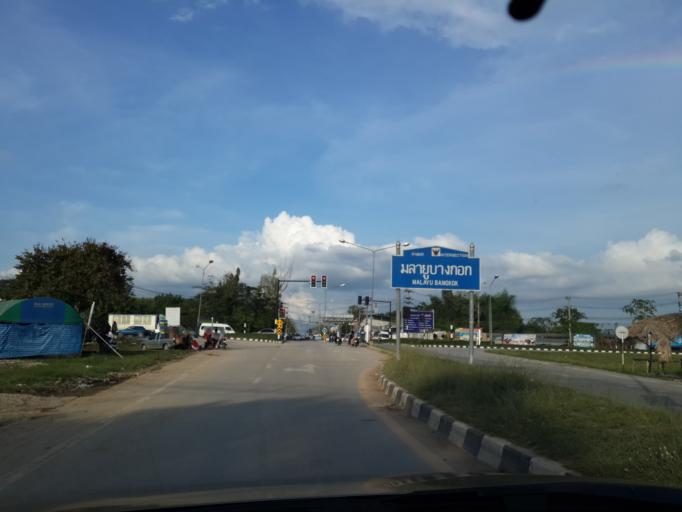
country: TH
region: Yala
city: Yala
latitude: 6.5132
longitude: 101.2723
